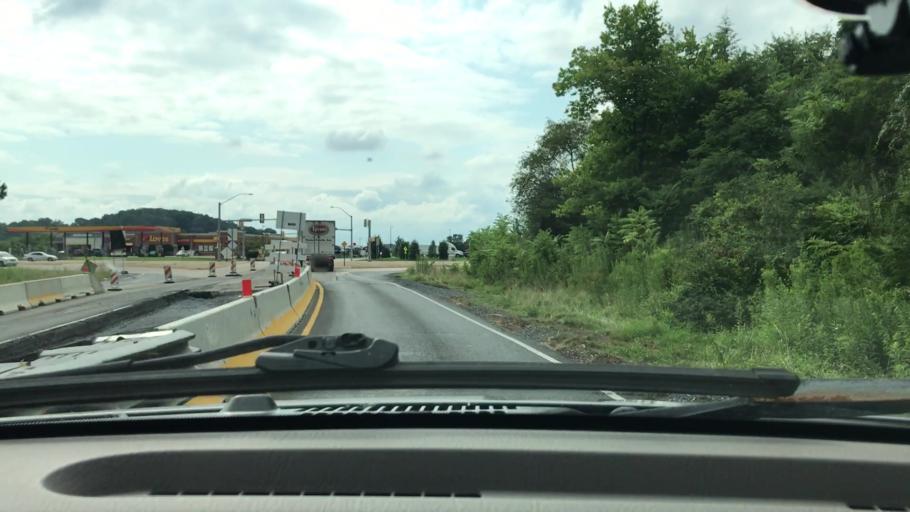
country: US
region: Pennsylvania
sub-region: Dauphin County
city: Middletown
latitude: 40.2264
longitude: -76.7177
